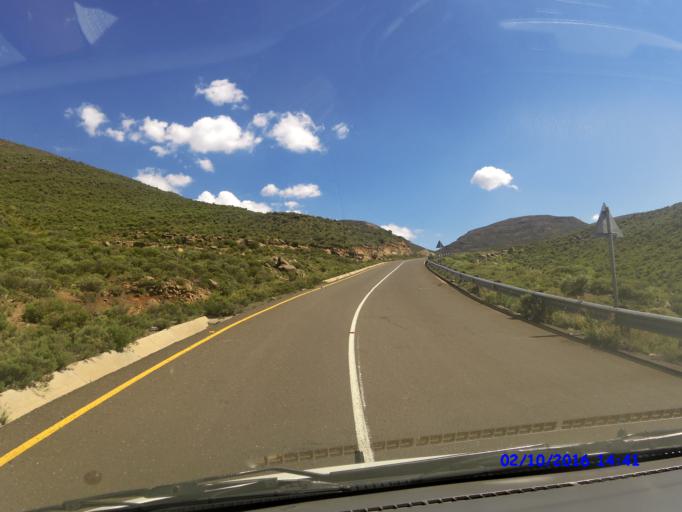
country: LS
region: Maseru
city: Nako
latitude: -29.5276
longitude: 28.0604
